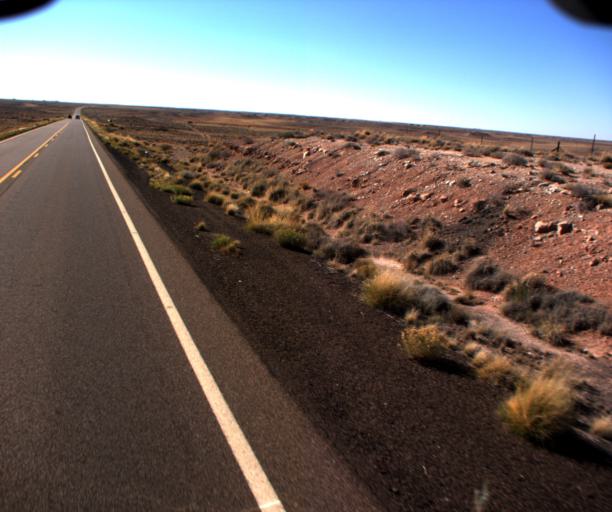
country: US
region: Arizona
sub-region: Navajo County
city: Dilkon
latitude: 35.2519
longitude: -110.4300
